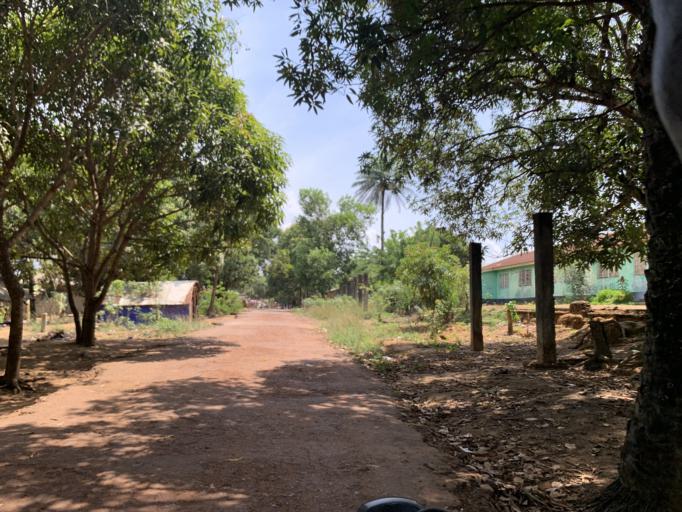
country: SL
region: Western Area
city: Waterloo
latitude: 8.3367
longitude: -13.0357
